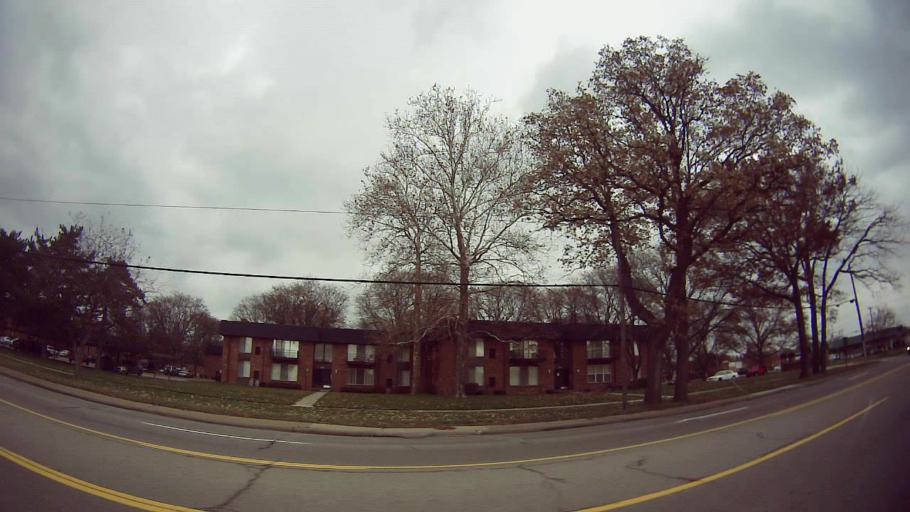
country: US
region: Michigan
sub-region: Macomb County
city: Center Line
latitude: 42.5034
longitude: -83.0067
